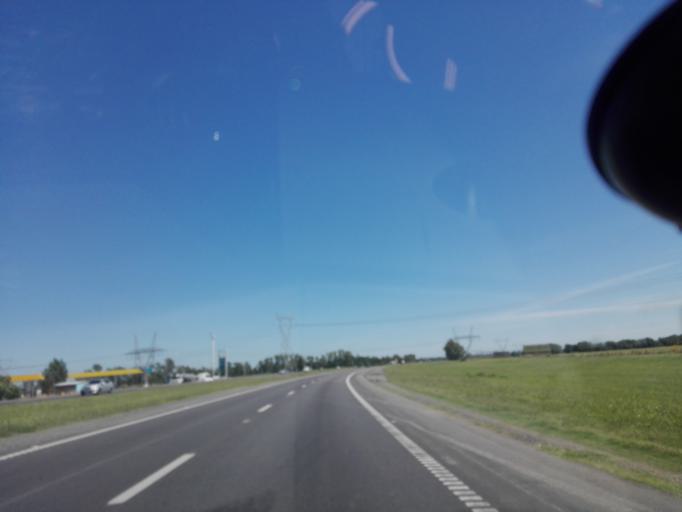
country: AR
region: Buenos Aires
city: San Nicolas de los Arroyos
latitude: -33.4314
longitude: -60.1745
